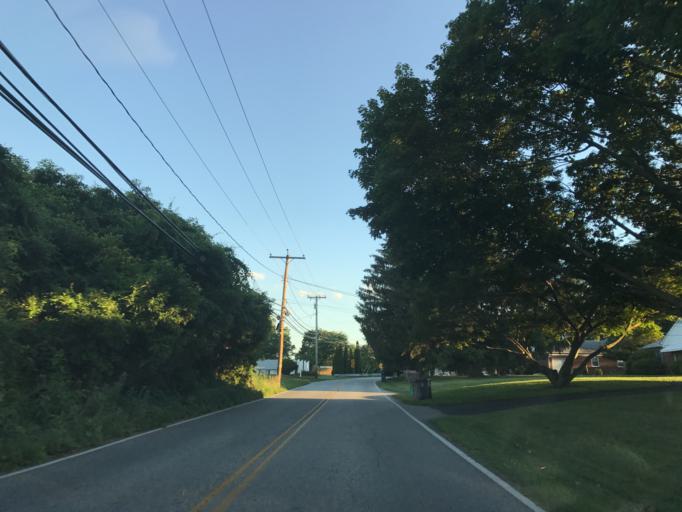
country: US
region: Maryland
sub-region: Harford County
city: Jarrettsville
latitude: 39.6015
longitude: -76.4835
